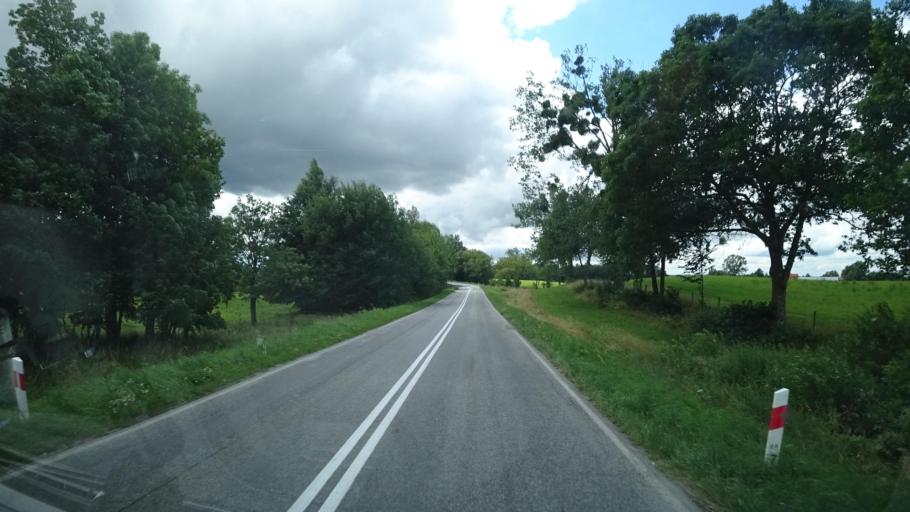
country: PL
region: Warmian-Masurian Voivodeship
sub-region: Powiat goldapski
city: Goldap
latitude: 54.2185
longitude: 22.2284
